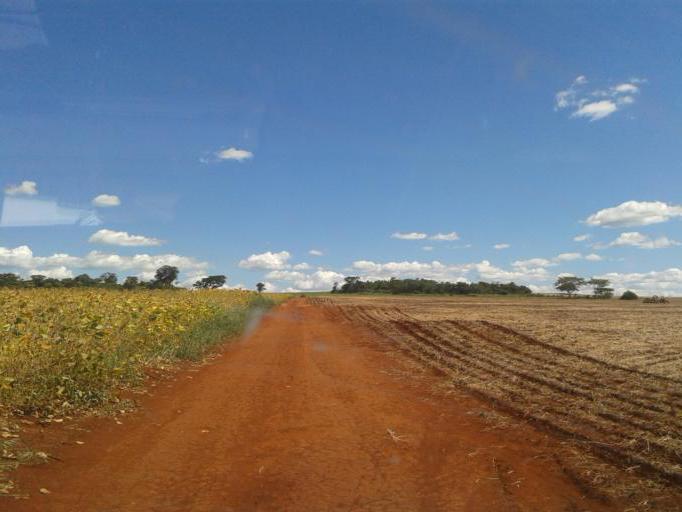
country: BR
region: Minas Gerais
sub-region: Capinopolis
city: Capinopolis
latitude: -18.6544
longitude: -49.5677
